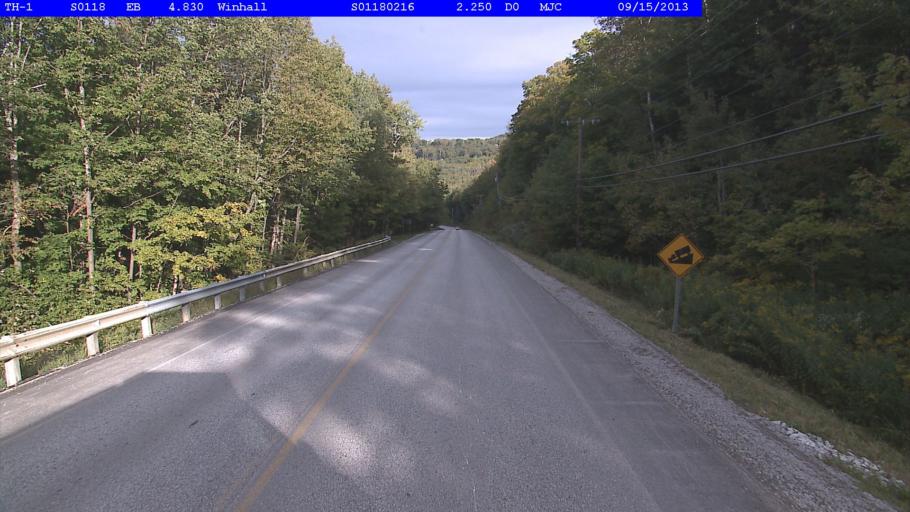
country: US
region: Vermont
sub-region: Bennington County
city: Manchester Center
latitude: 43.1351
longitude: -72.8897
